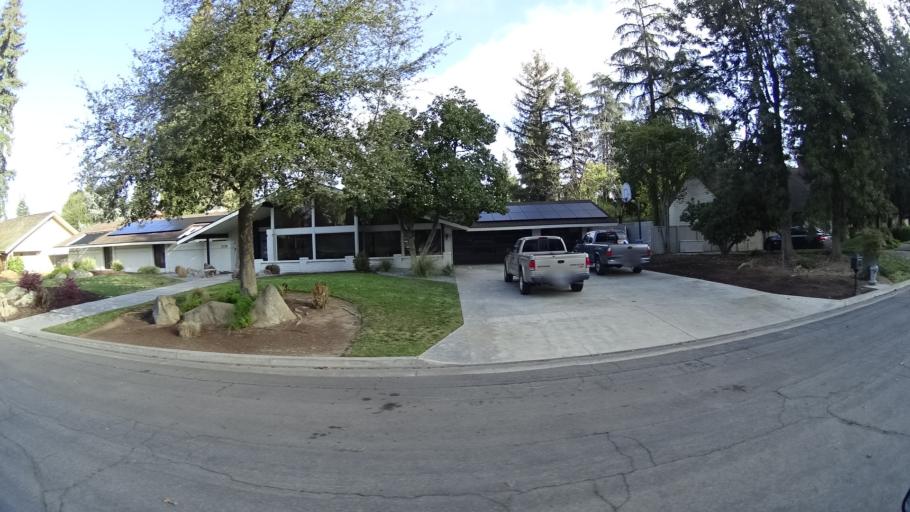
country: US
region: California
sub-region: Fresno County
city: Fresno
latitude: 36.8141
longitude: -119.8298
